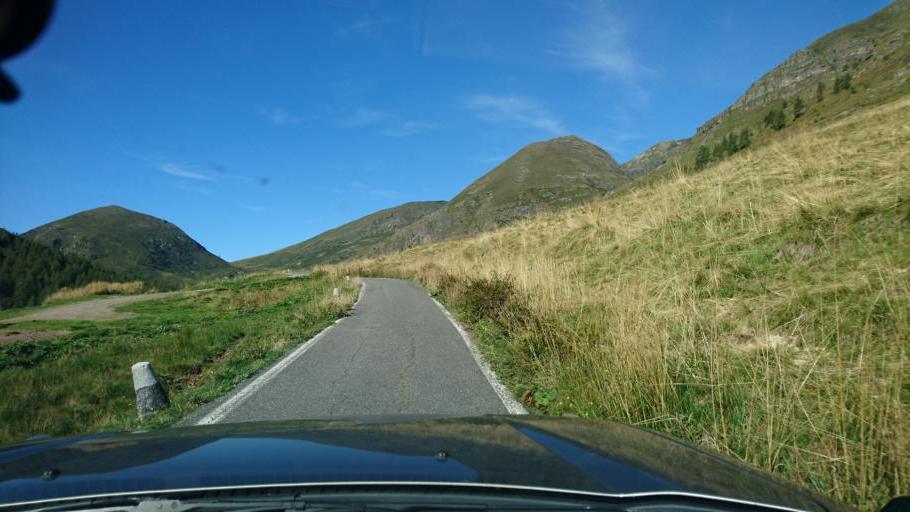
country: IT
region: Lombardy
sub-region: Provincia di Bergamo
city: Schilpario
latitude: 46.0384
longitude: 10.2071
